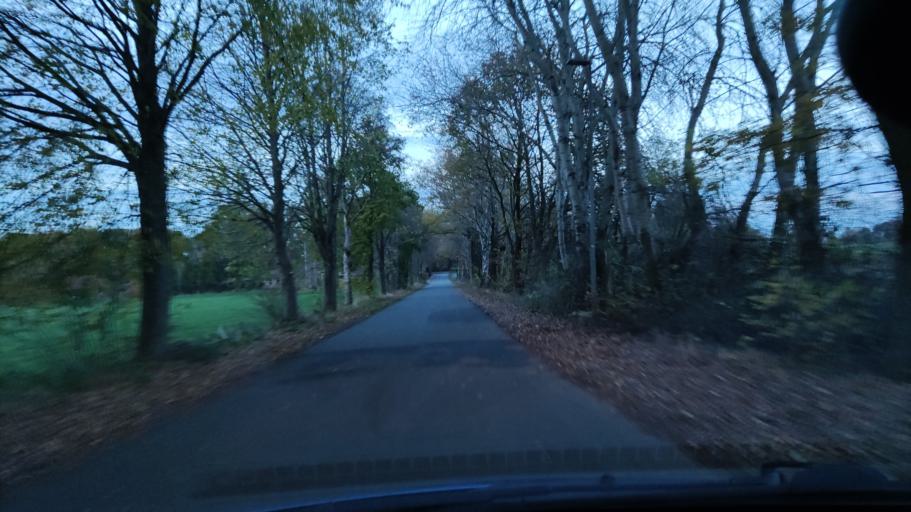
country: DE
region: Lower Saxony
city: Bispingen
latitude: 53.1389
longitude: 10.0259
